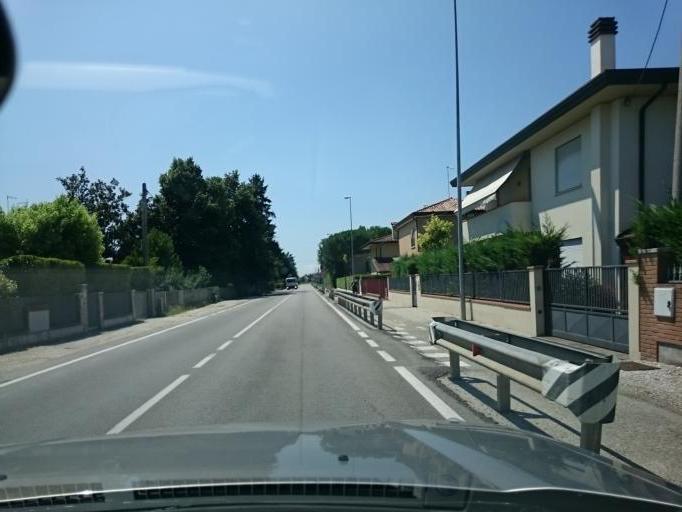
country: IT
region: Veneto
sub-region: Provincia di Padova
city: Sarmeola
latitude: 45.4332
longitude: 11.8272
